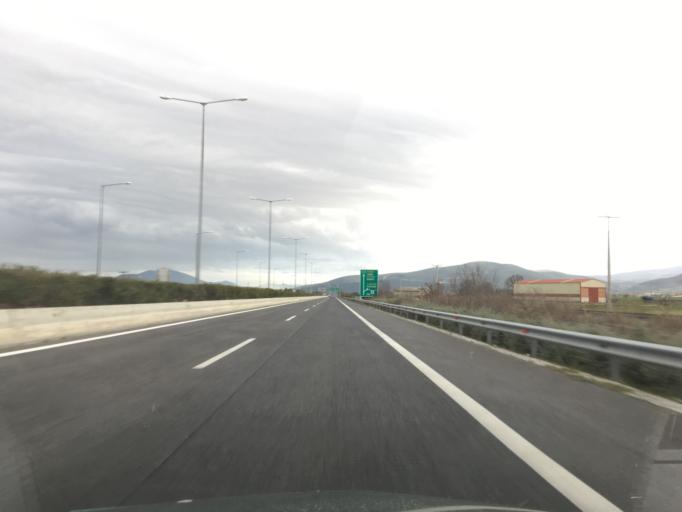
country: GR
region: Thessaly
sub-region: Nomos Magnisias
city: Almyros
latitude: 39.2012
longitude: 22.7615
